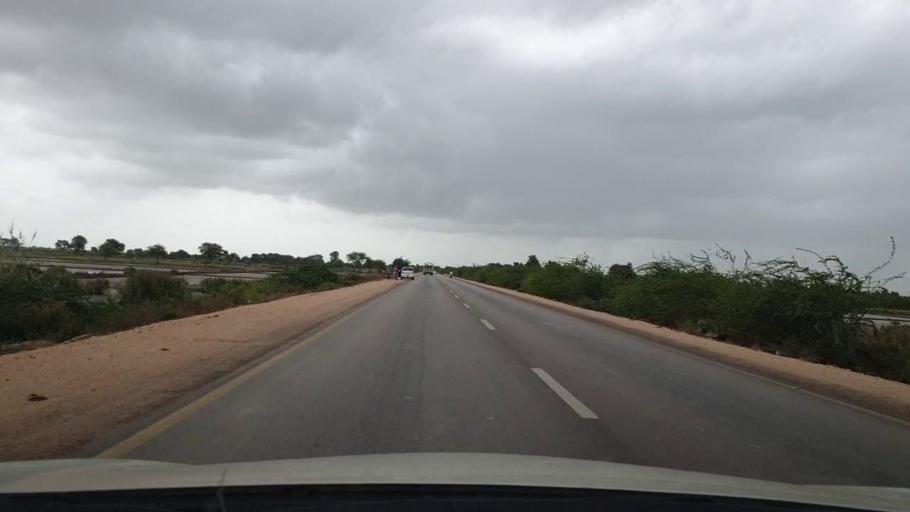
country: PK
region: Sindh
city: Mirpur Batoro
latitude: 24.6427
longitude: 68.4589
